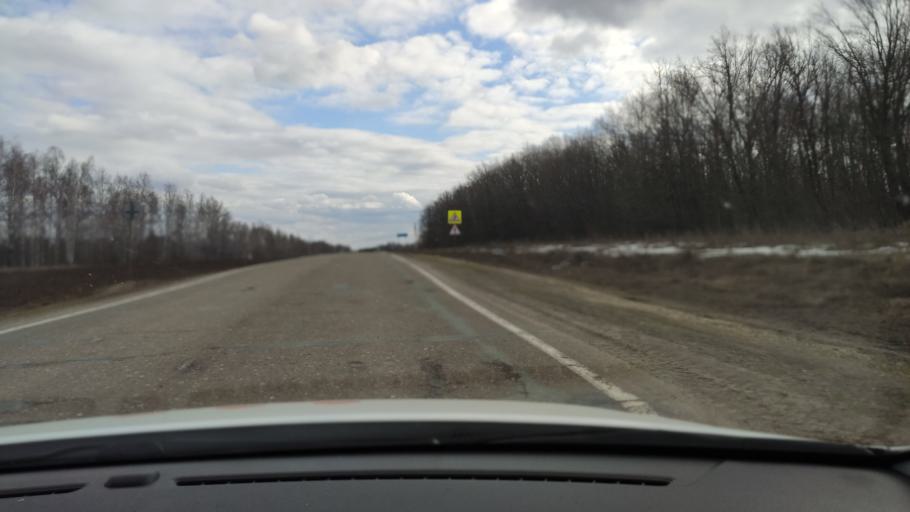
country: RU
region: Tatarstan
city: Vysokaya Gora
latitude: 56.0782
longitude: 49.1879
